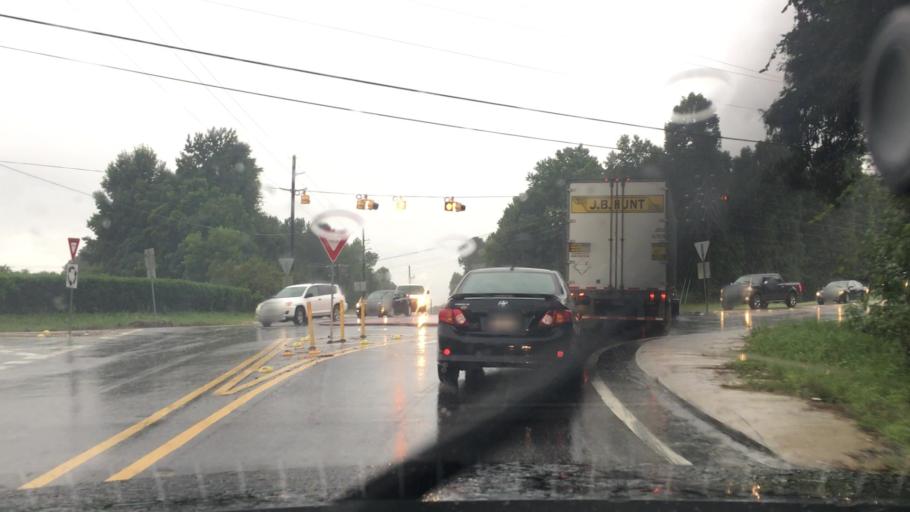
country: US
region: Georgia
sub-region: Fayette County
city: Peachtree City
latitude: 33.3297
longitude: -84.6445
